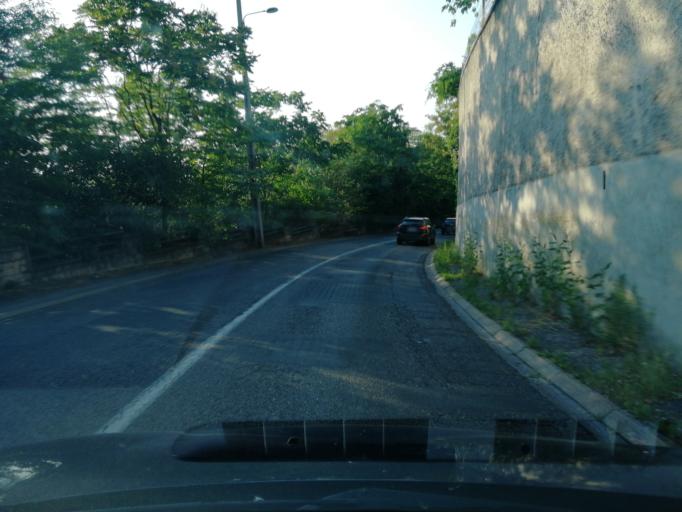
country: FR
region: Rhone-Alpes
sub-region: Departement du Rhone
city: Sathonay-Camp
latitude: 45.8238
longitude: 4.8611
